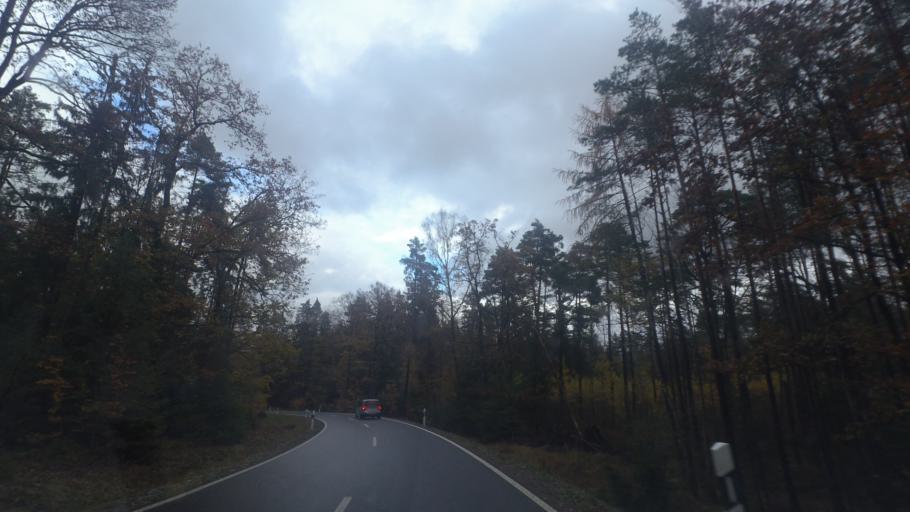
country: DE
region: Bavaria
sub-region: Regierungsbezirk Unterfranken
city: Oberelsbach
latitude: 50.3715
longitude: 10.1019
